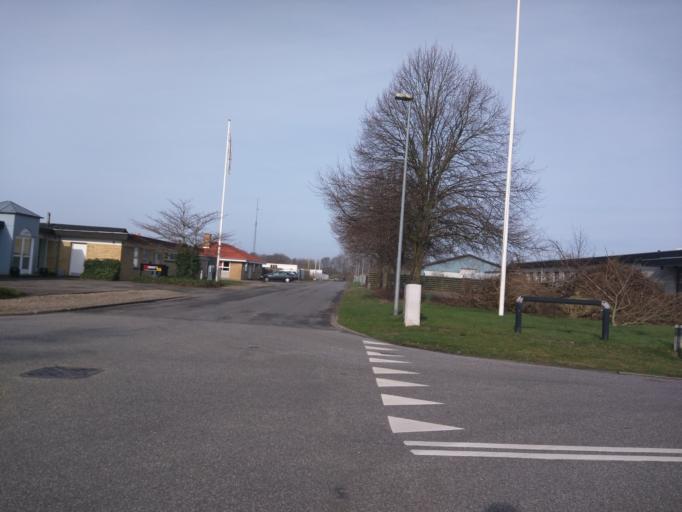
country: DK
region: South Denmark
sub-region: Fredericia Kommune
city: Snoghoj
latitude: 55.5476
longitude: 9.6916
